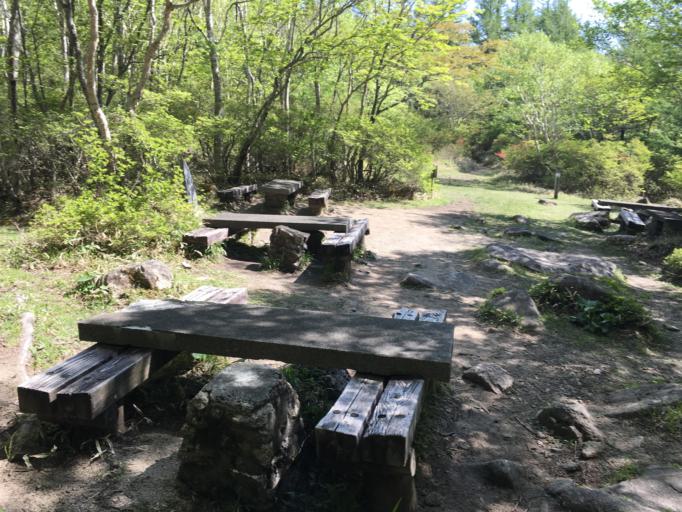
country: JP
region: Iwate
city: Ofunato
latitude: 39.1883
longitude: 141.7313
